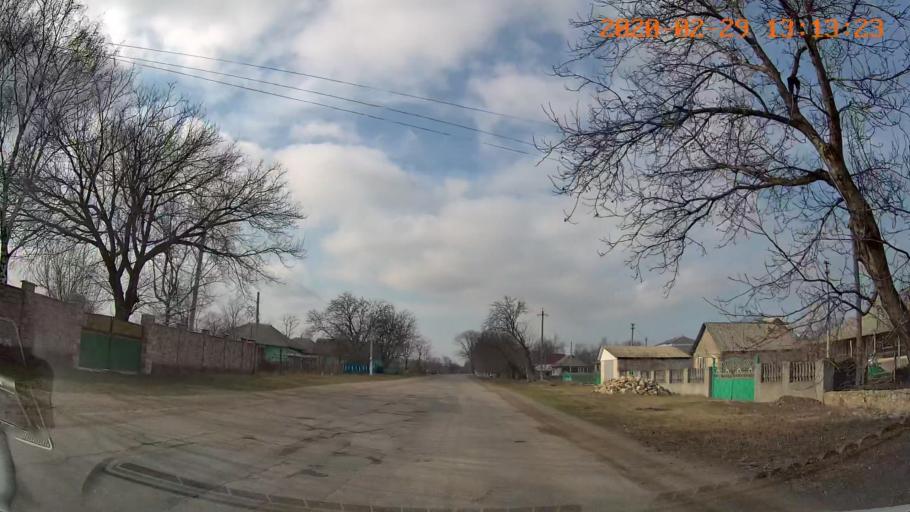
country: MD
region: Telenesti
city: Camenca
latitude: 48.0142
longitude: 28.6848
